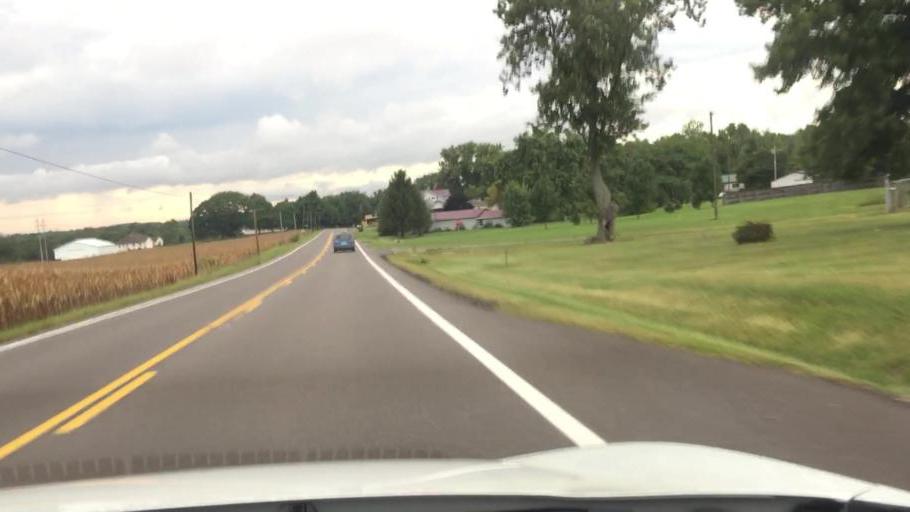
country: US
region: Ohio
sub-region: Champaign County
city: Mechanicsburg
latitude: 40.0637
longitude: -83.5437
